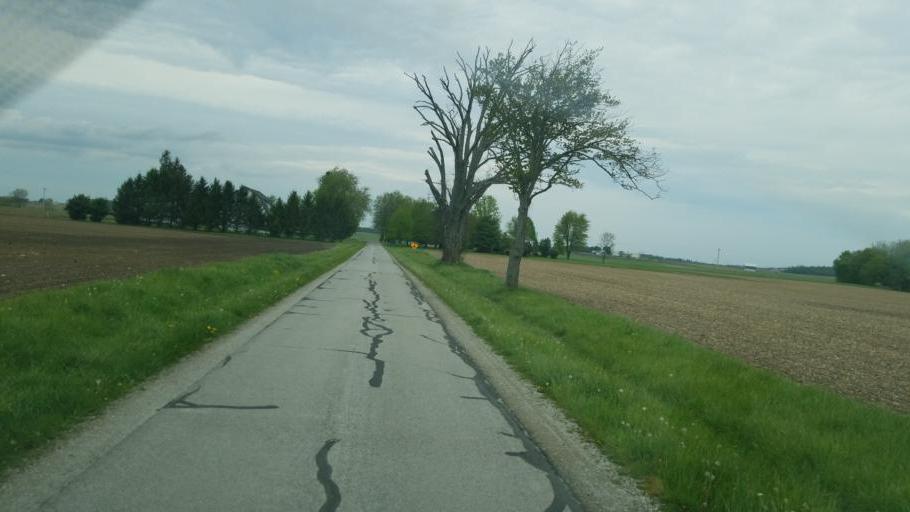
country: US
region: Ohio
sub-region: Huron County
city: Willard
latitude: 41.0417
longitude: -82.8619
